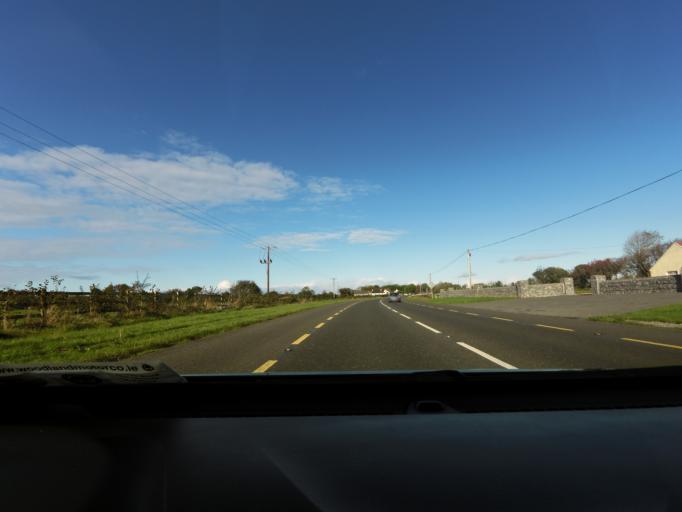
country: IE
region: Connaught
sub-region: County Galway
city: Moycullen
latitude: 53.4423
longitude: -9.0806
